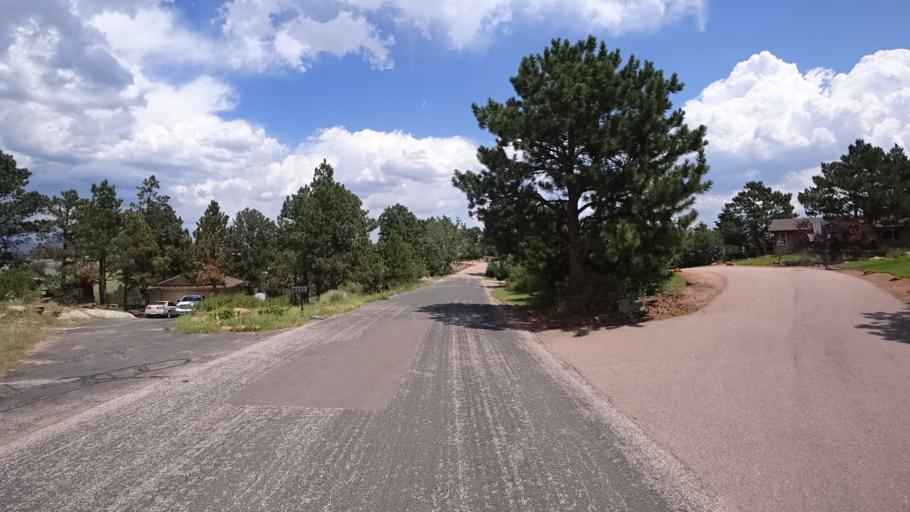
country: US
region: Colorado
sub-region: El Paso County
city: Air Force Academy
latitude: 38.9403
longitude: -104.8103
